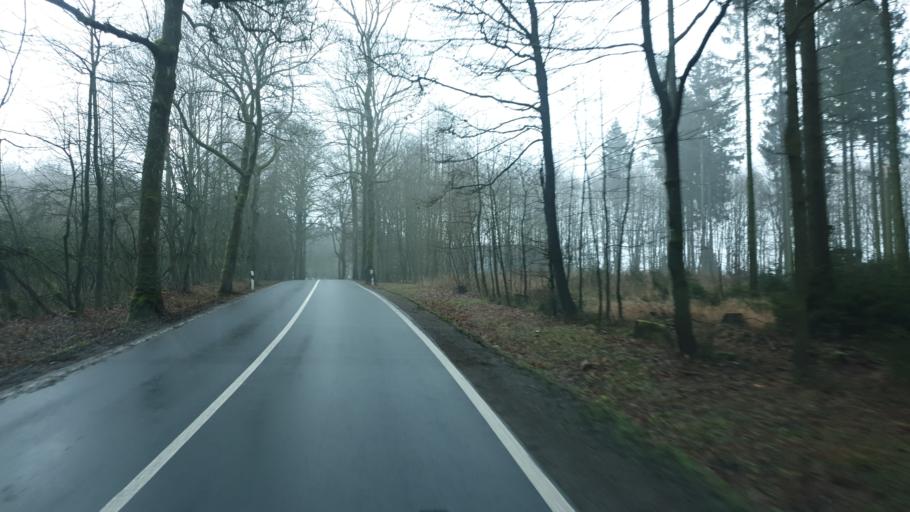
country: DE
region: Saxony
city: Neuhausen
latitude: 50.6951
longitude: 13.4530
